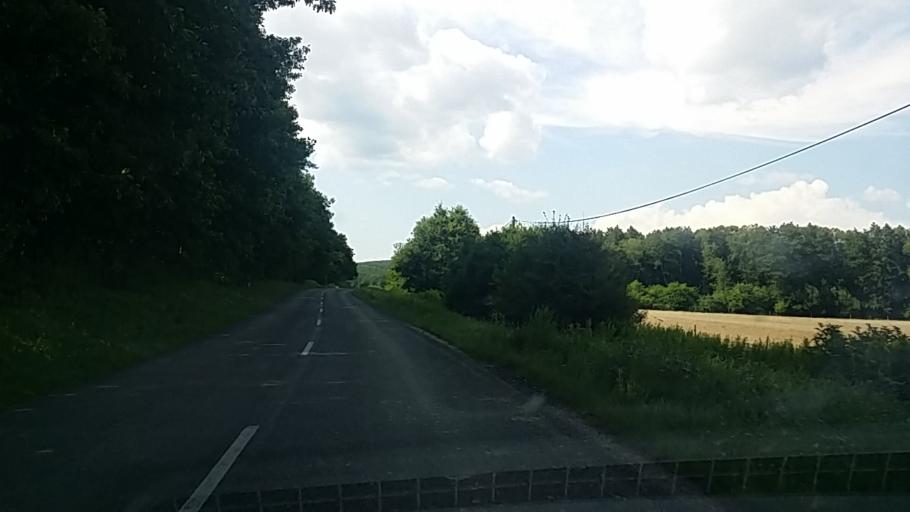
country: HU
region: Zala
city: Becsehely
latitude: 46.4576
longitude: 16.8108
